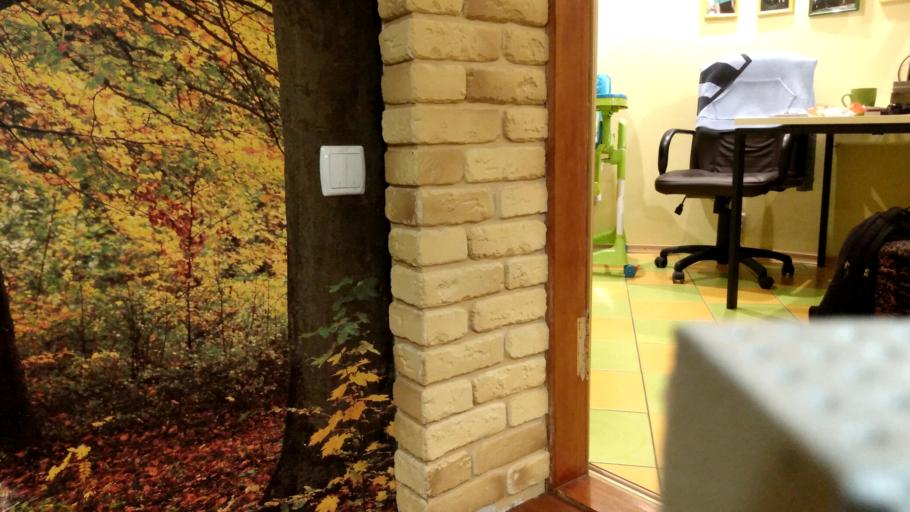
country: RU
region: Republic of Karelia
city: Pudozh
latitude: 61.7794
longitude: 37.6792
